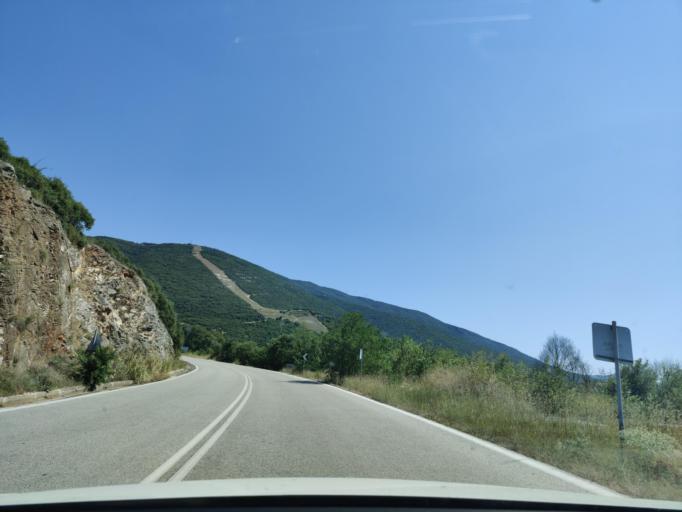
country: GR
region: East Macedonia and Thrace
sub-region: Nomos Kavalas
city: Zygos
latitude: 40.9989
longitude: 24.3804
